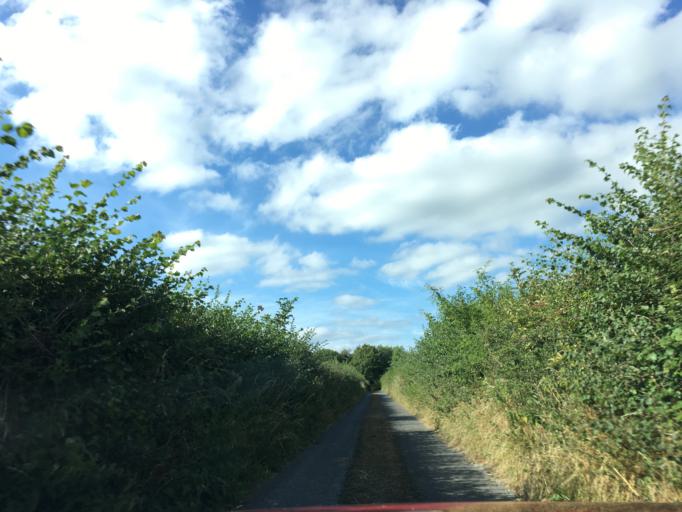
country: IE
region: Munster
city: Cashel
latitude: 52.4604
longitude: -7.9417
